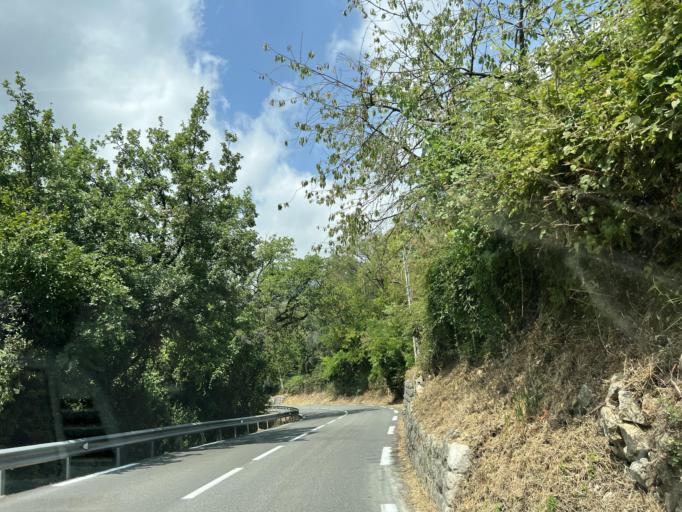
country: FR
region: Provence-Alpes-Cote d'Azur
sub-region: Departement des Alpes-Maritimes
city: Le Rouret
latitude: 43.7040
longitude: 7.0129
